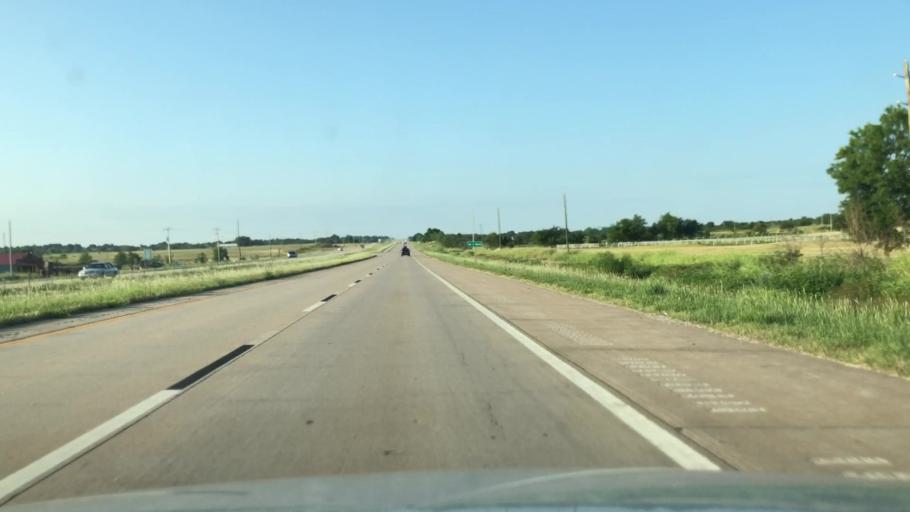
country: US
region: Oklahoma
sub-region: Osage County
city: Skiatook
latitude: 36.4552
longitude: -95.9207
